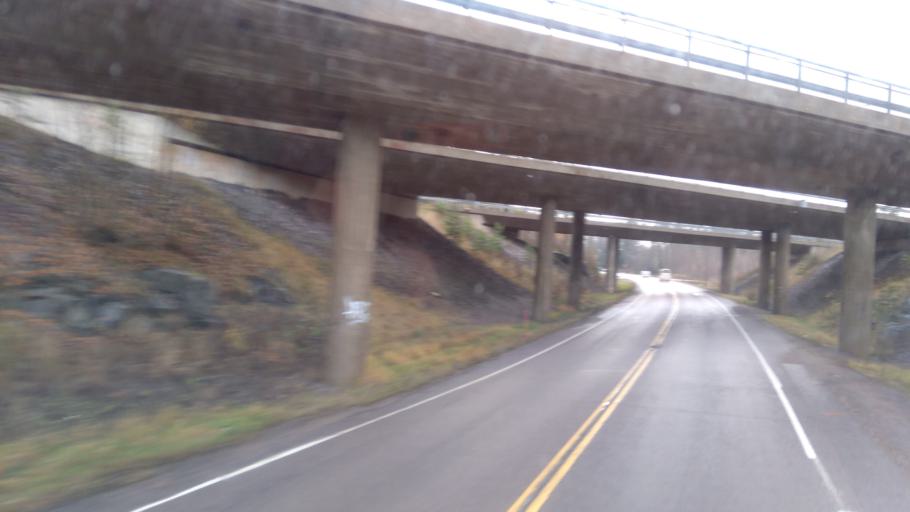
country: FI
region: Uusimaa
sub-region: Porvoo
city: Porvoo
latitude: 60.4194
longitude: 25.7067
